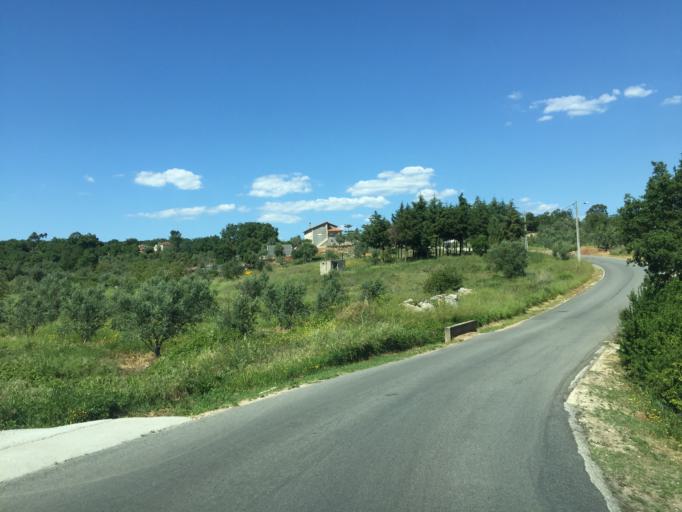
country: PT
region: Leiria
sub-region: Alvaiazere
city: Alvaiazere
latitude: 39.8165
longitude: -8.4005
